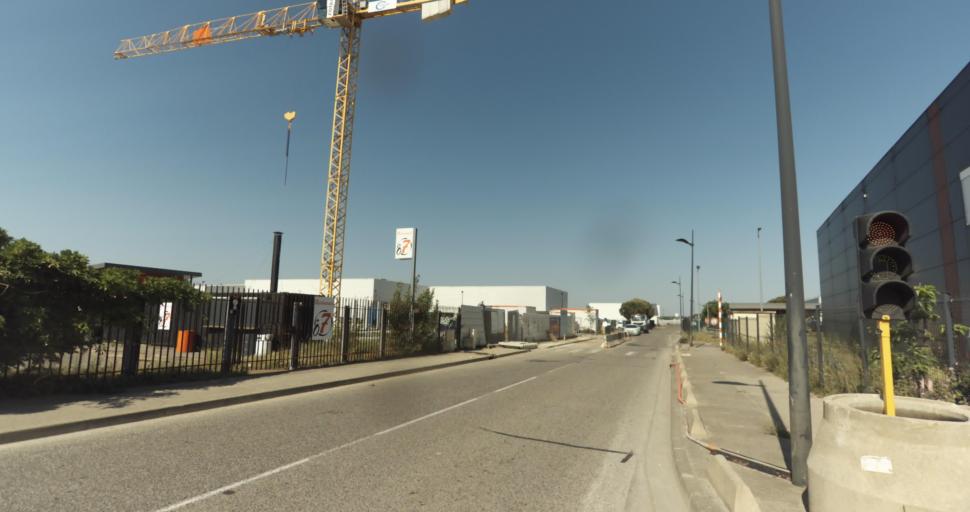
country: FR
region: Midi-Pyrenees
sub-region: Departement de la Haute-Garonne
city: Tournefeuille
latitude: 43.5914
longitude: 1.2977
